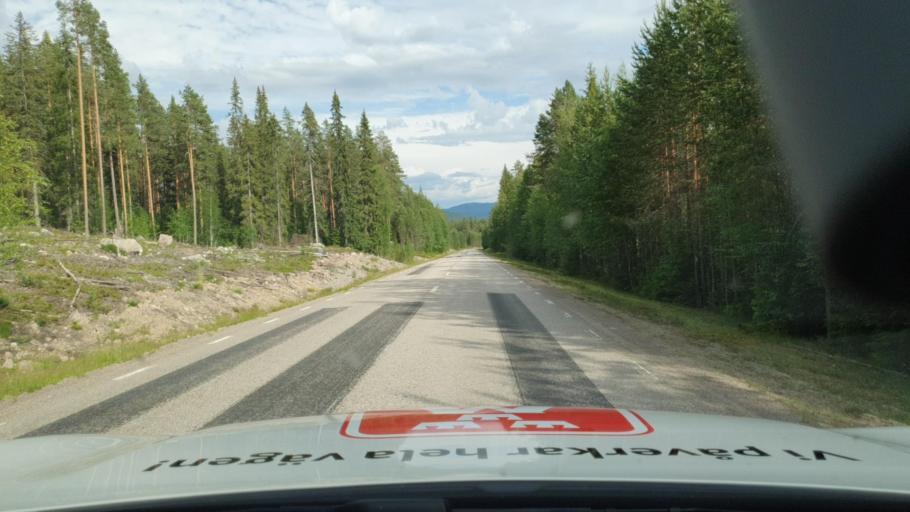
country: NO
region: Hedmark
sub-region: Trysil
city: Innbygda
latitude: 60.9305
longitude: 12.5015
